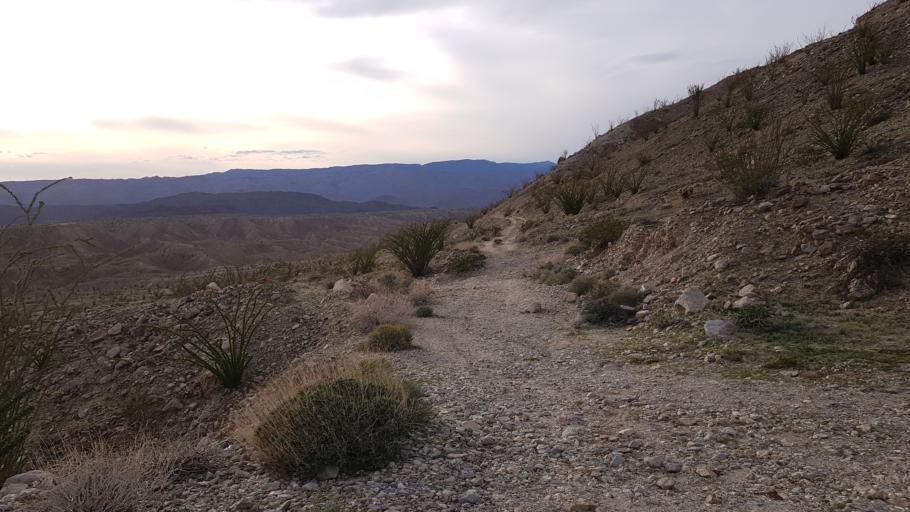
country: MX
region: Baja California
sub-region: Tecate
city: Cereso del Hongo
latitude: 32.8260
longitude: -116.1340
